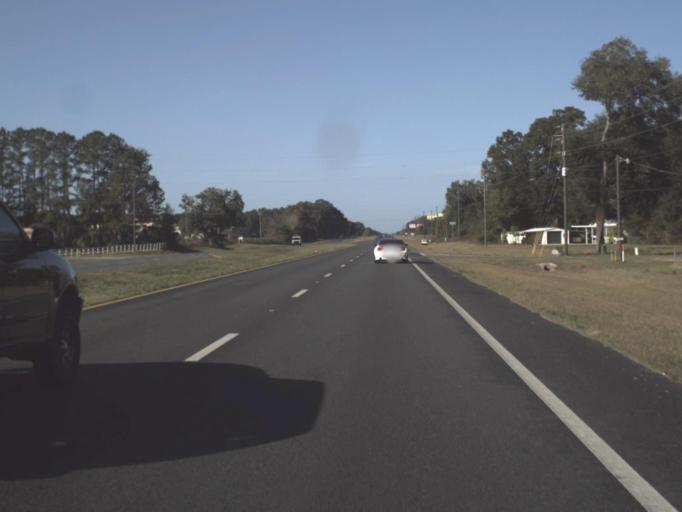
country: US
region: Florida
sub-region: Marion County
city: Belleview
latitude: 29.0261
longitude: -82.0912
